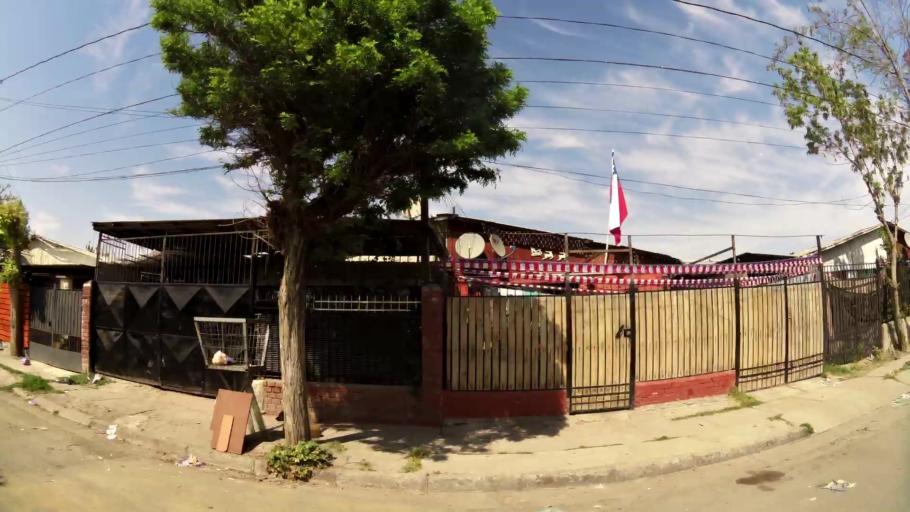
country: CL
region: Santiago Metropolitan
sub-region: Provincia de Santiago
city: La Pintana
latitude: -33.5591
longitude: -70.6395
